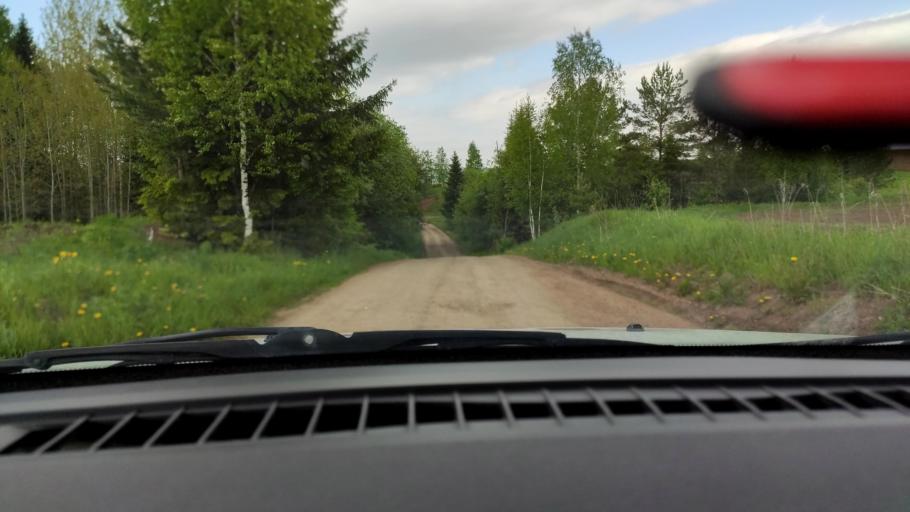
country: RU
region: Perm
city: Bershet'
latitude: 57.7232
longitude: 56.3978
